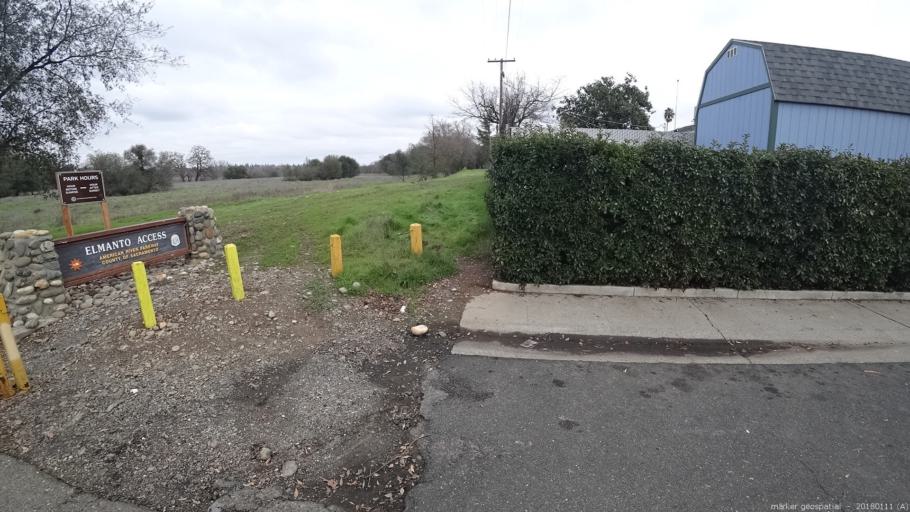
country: US
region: California
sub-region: Sacramento County
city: Fair Oaks
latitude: 38.6186
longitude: -121.2868
